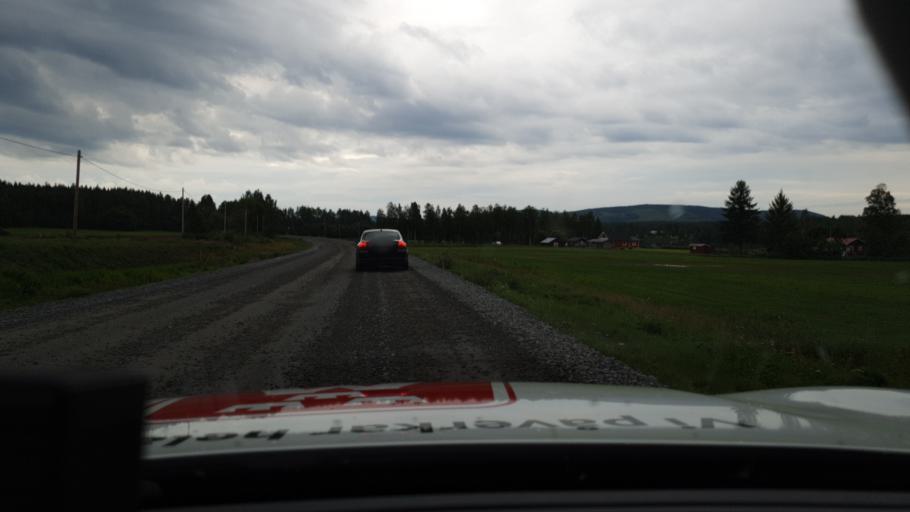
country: SE
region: Norrbotten
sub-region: Bodens Kommun
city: Boden
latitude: 65.8664
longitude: 21.4164
